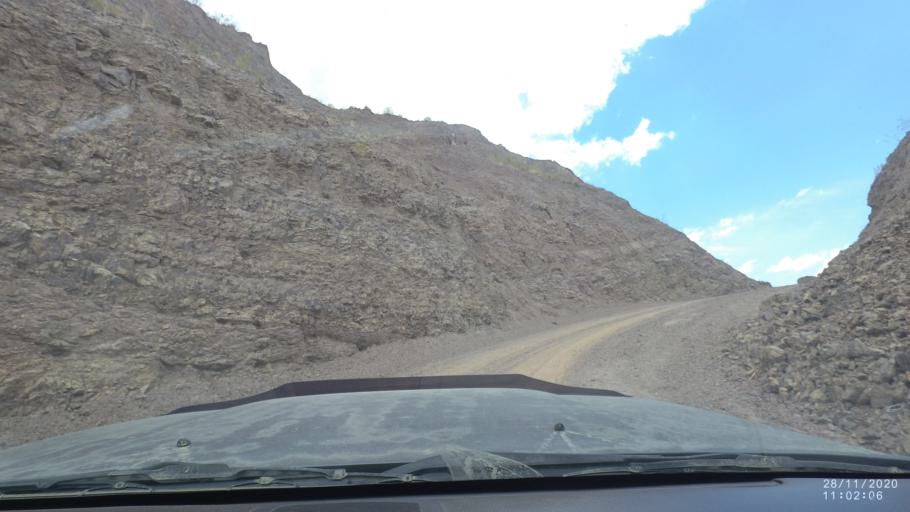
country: BO
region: Cochabamba
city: Capinota
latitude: -17.7648
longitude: -66.1050
